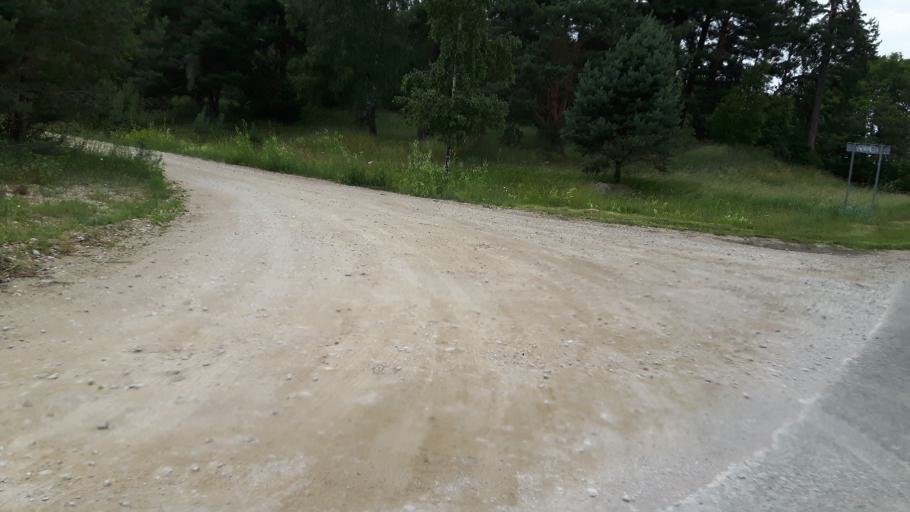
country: LV
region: Liepaja
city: Vec-Liepaja
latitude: 56.5882
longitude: 21.0275
